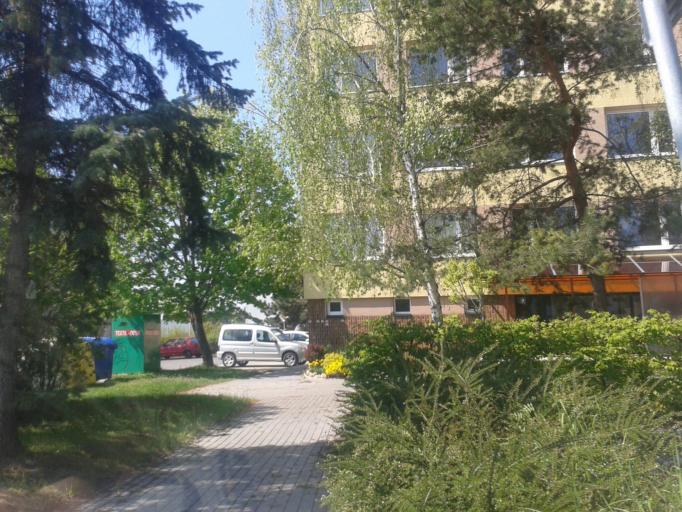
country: CZ
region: Central Bohemia
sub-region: Okres Beroun
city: Kraluv Dvur
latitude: 49.9494
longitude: 14.0373
